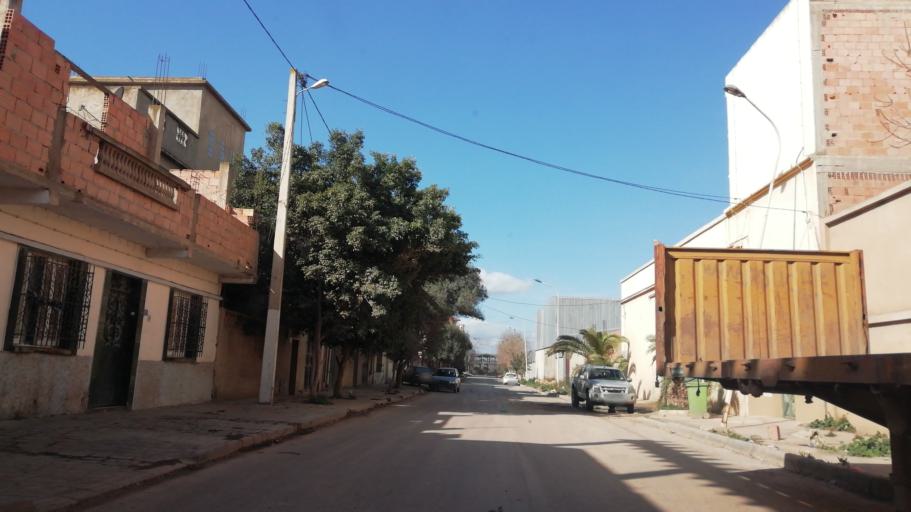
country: DZ
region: Oran
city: Es Senia
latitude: 35.6231
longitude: -0.5817
